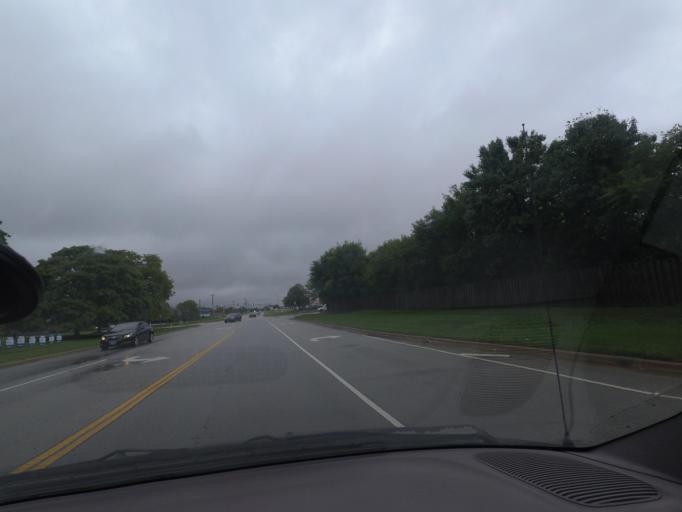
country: US
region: Illinois
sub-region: Champaign County
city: Champaign
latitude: 40.1167
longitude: -88.2817
